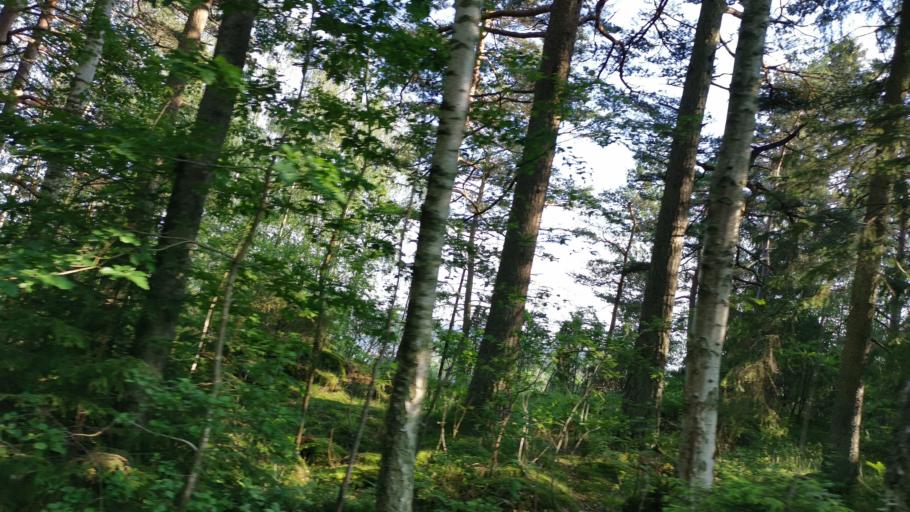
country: SE
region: Vaestra Goetaland
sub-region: Orust
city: Henan
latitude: 58.2861
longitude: 11.6567
